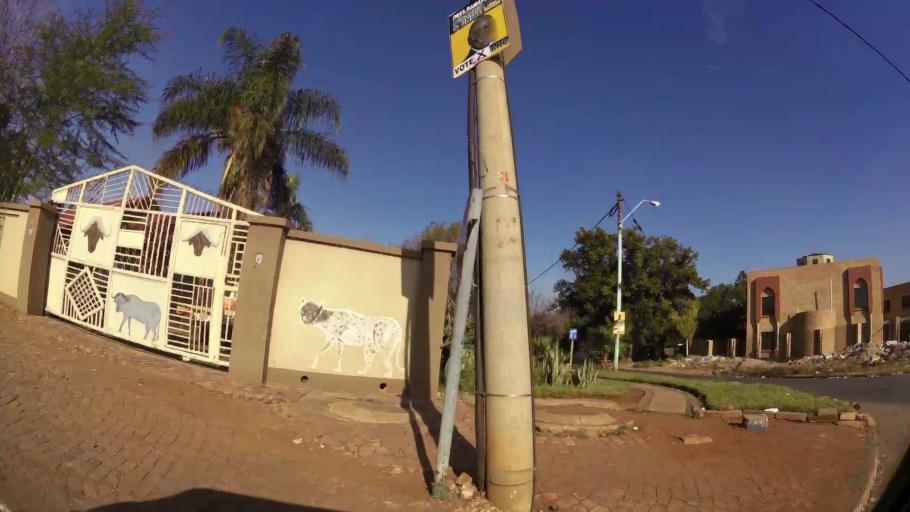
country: ZA
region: North-West
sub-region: Bojanala Platinum District Municipality
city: Rustenburg
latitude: -25.6517
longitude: 27.2498
